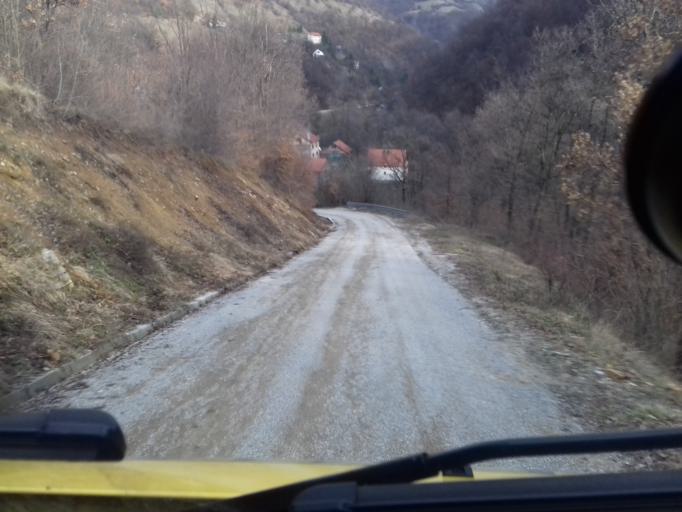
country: BA
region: Federation of Bosnia and Herzegovina
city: Zenica
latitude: 44.2330
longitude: 17.9930
